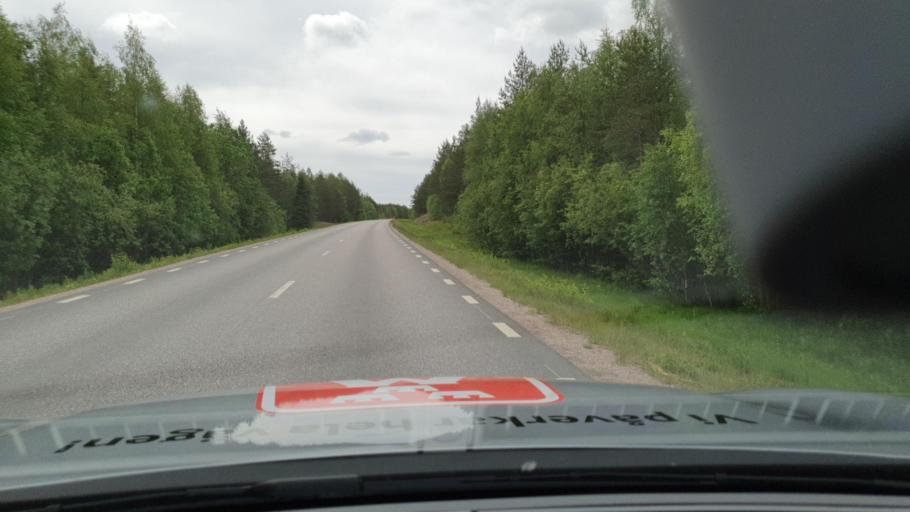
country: SE
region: Norrbotten
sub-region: Kalix Kommun
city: Kalix
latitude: 65.8634
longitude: 23.4833
